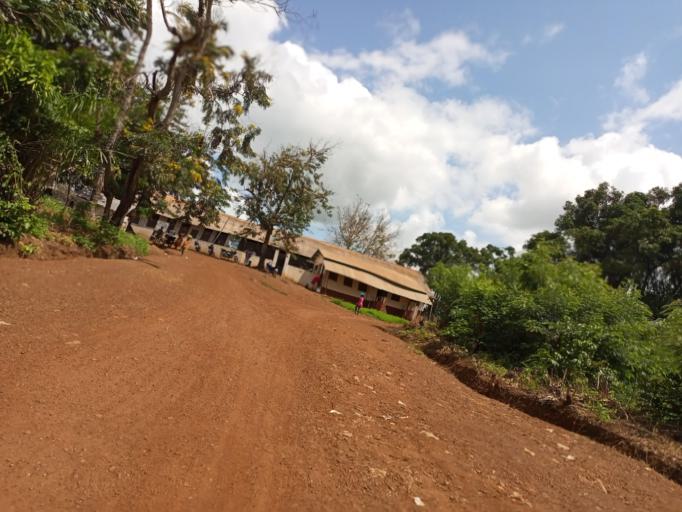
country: SL
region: Northern Province
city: Kamakwie
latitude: 9.4978
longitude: -12.2376
